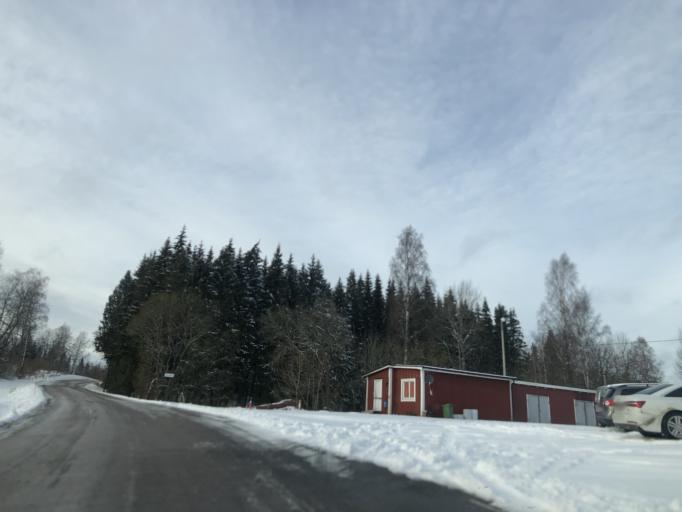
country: SE
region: Vaestra Goetaland
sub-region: Ulricehamns Kommun
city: Ulricehamn
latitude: 57.8096
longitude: 13.5419
